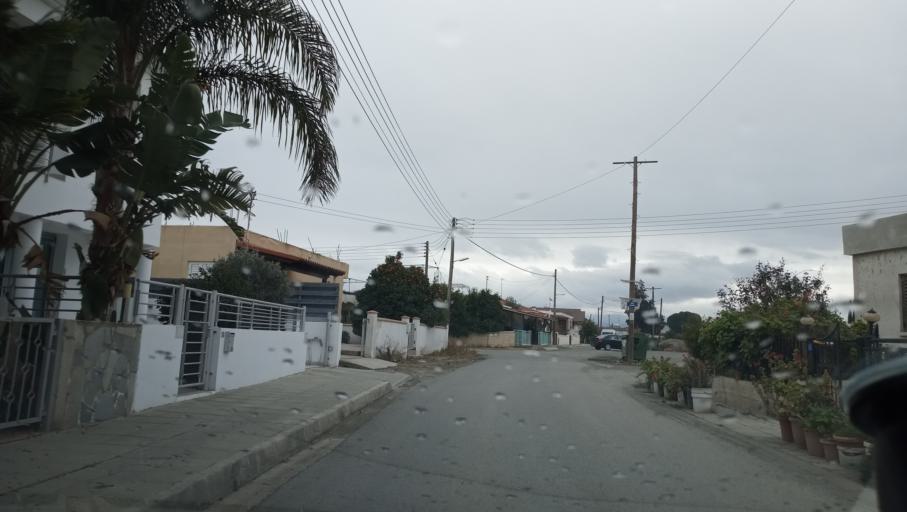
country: CY
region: Lefkosia
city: Kato Deftera
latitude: 35.0838
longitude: 33.2732
